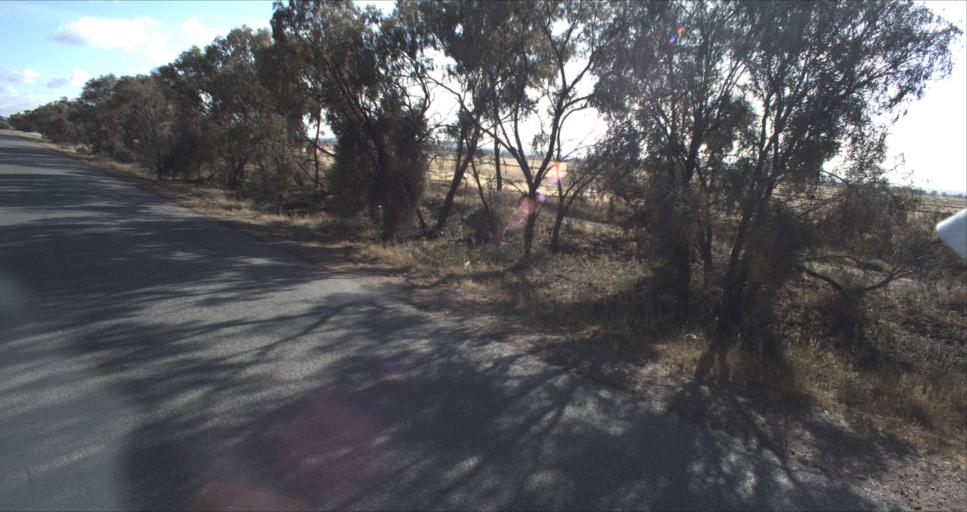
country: AU
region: New South Wales
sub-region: Leeton
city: Leeton
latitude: -34.5159
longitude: 146.3915
